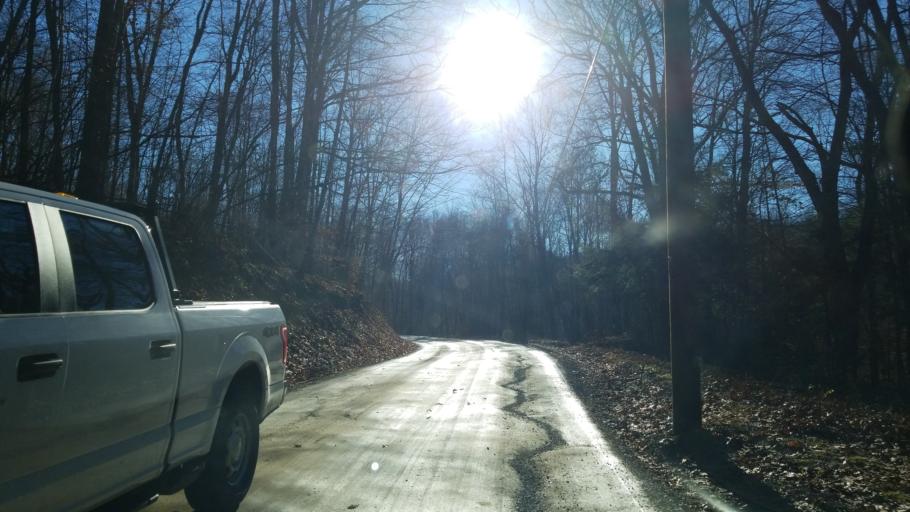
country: US
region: Pennsylvania
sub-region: Jefferson County
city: Falls Creek
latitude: 41.1343
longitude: -78.7891
